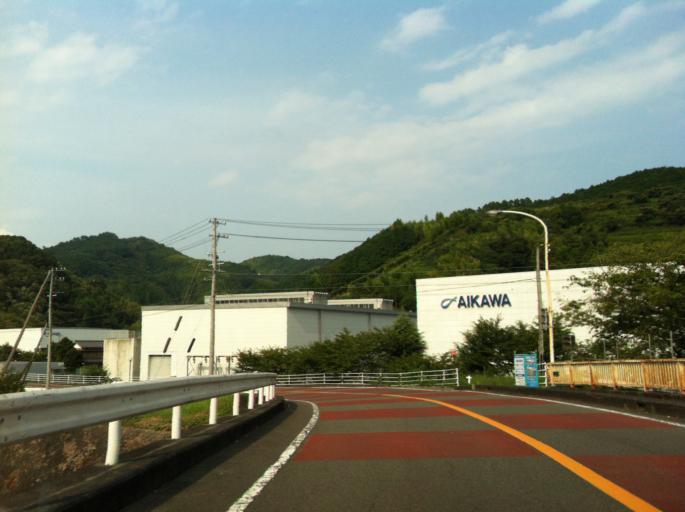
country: JP
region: Shizuoka
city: Fujieda
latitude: 34.9201
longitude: 138.2708
